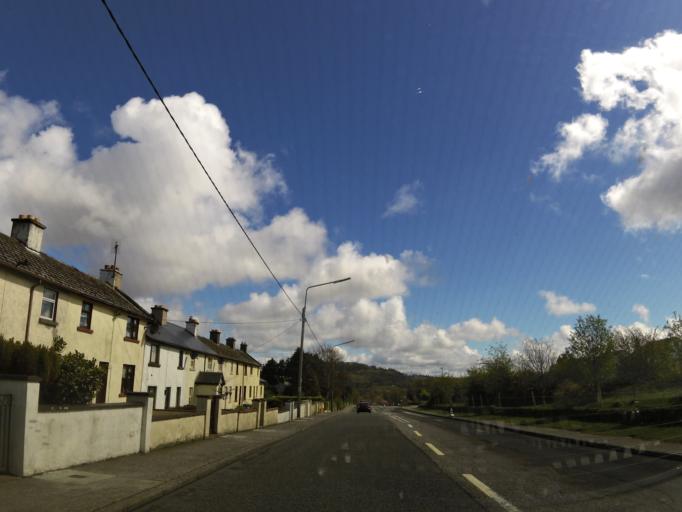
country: IE
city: Ballisodare
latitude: 54.2109
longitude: -8.5159
